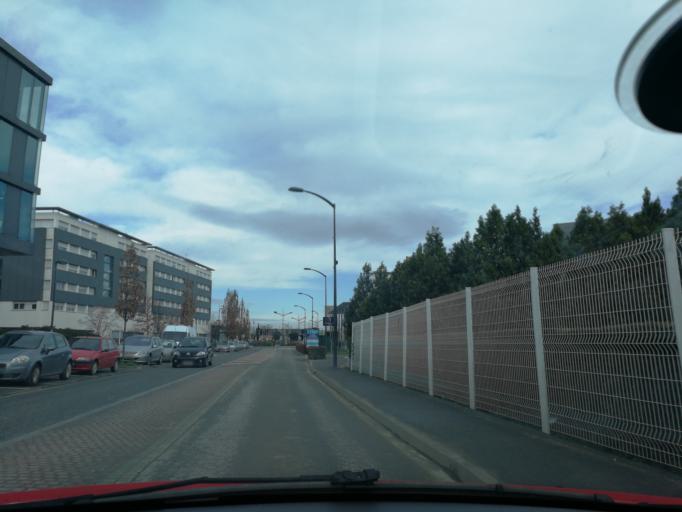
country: FR
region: Midi-Pyrenees
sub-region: Departement de la Haute-Garonne
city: Balma
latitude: 43.6263
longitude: 1.4845
